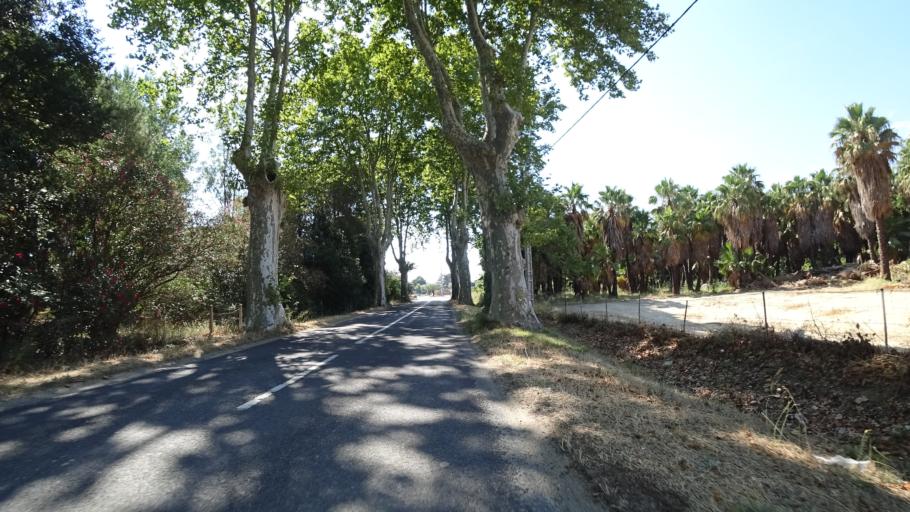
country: FR
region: Languedoc-Roussillon
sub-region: Departement des Pyrenees-Orientales
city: Bompas
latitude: 42.7273
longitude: 2.9456
